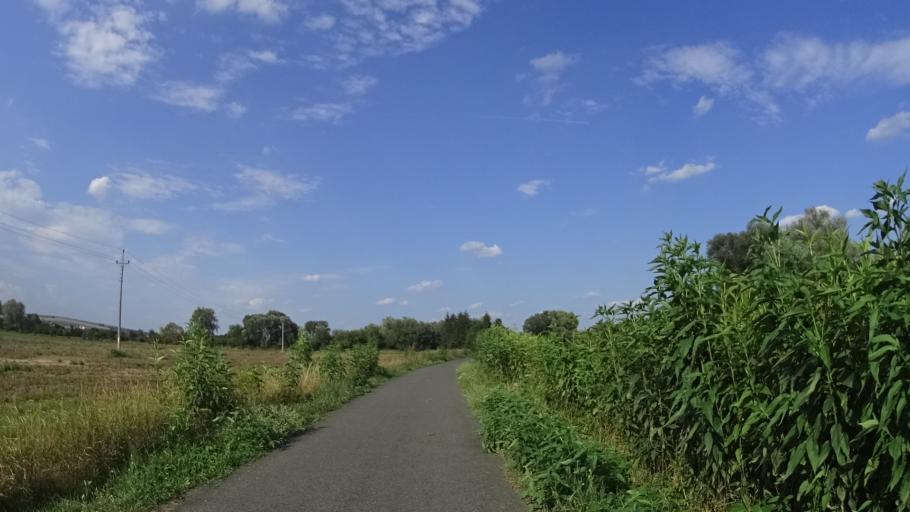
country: CZ
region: Zlin
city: Babice
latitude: 49.1234
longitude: 17.4899
